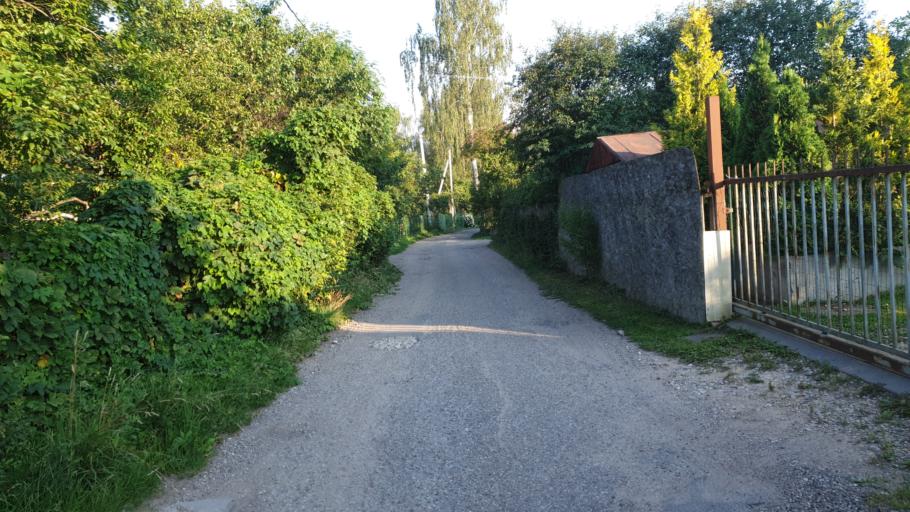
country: LT
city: Grigiskes
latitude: 54.7641
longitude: 25.0297
